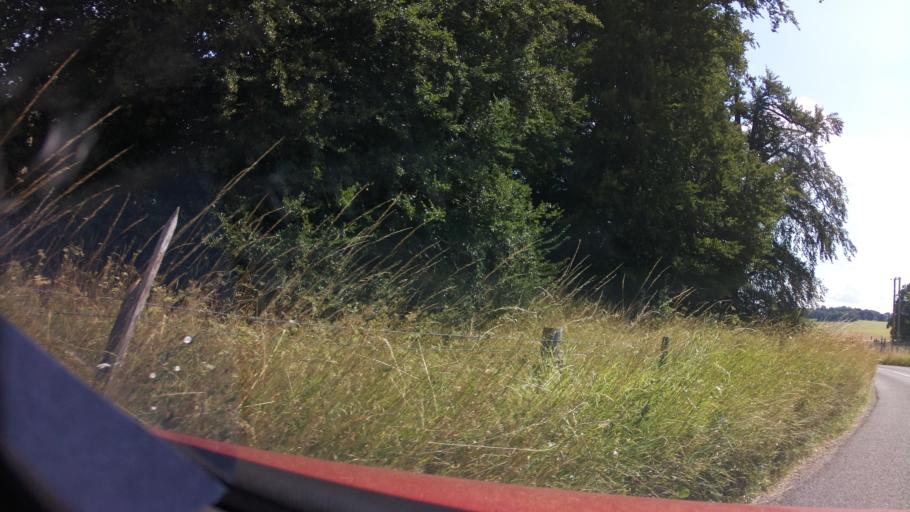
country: GB
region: England
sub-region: Wiltshire
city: Aldbourne
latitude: 51.5298
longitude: -1.5863
